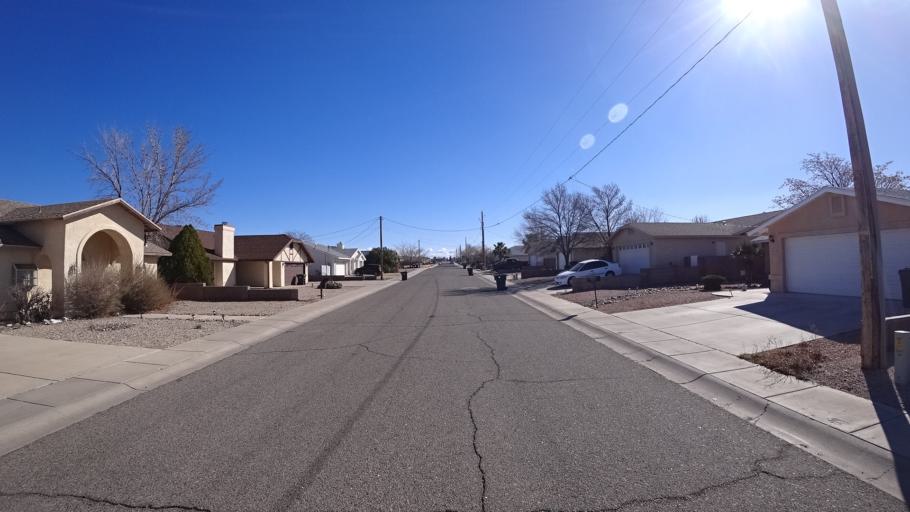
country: US
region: Arizona
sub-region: Mohave County
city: Kingman
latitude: 35.1965
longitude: -114.0172
